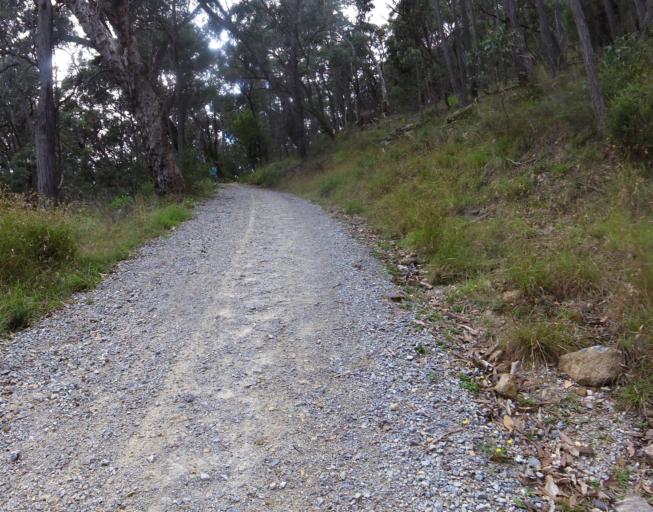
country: AU
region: Victoria
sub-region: Yarra Ranges
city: Montrose
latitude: -37.8253
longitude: 145.3470
